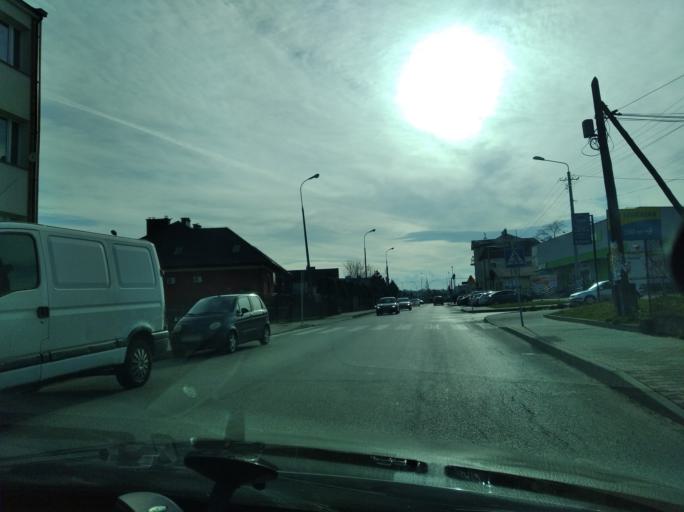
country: PL
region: Subcarpathian Voivodeship
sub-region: Powiat ropczycko-sedziszowski
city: Sedziszow Malopolski
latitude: 50.0704
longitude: 21.6895
